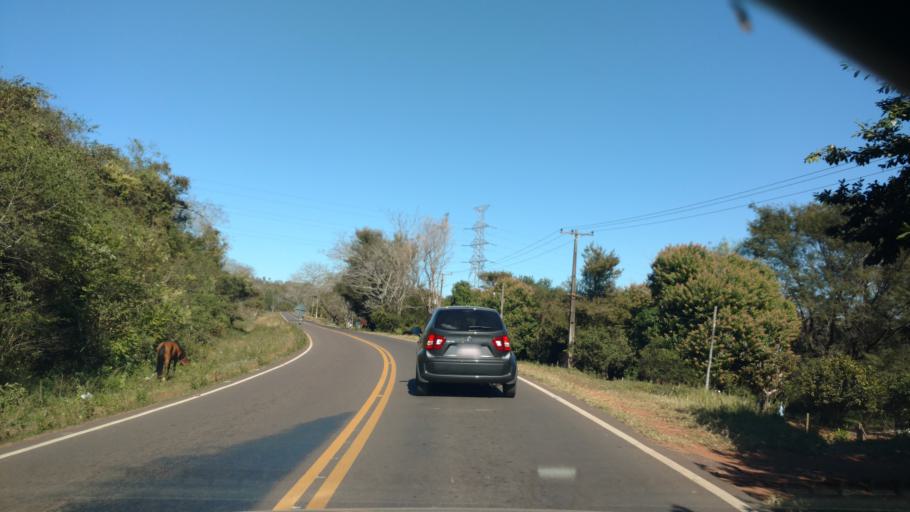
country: PY
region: Paraguari
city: Pirayu
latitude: -25.4949
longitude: -57.2453
